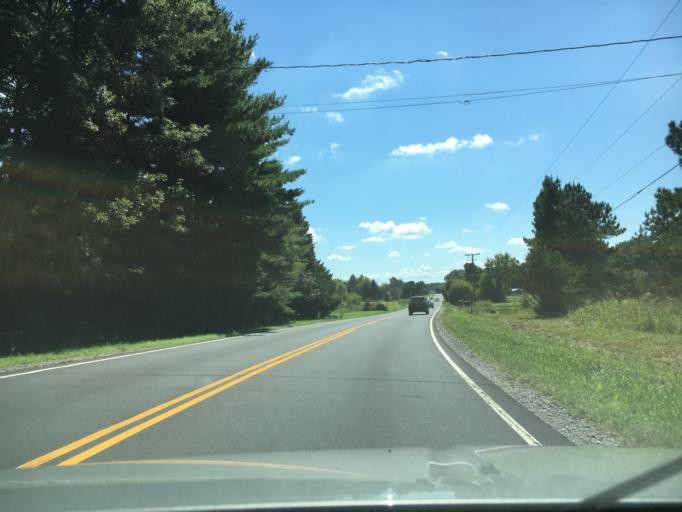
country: US
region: Virginia
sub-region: Amelia County
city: Amelia Court House
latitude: 37.3795
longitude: -77.9004
